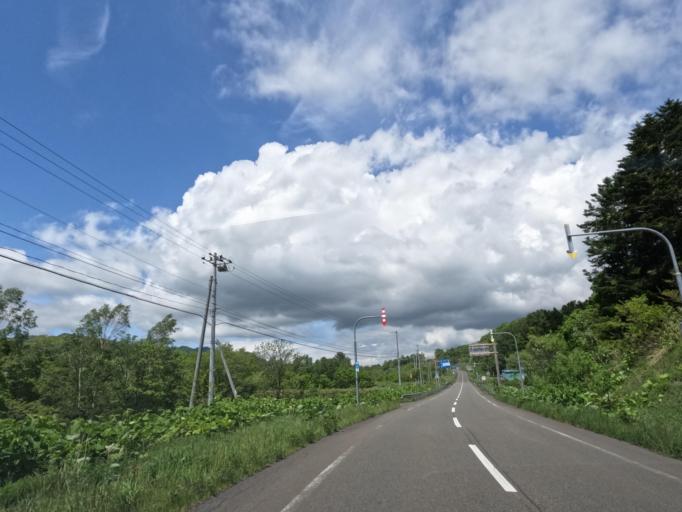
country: JP
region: Hokkaido
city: Tobetsu
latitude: 43.4207
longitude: 141.5794
